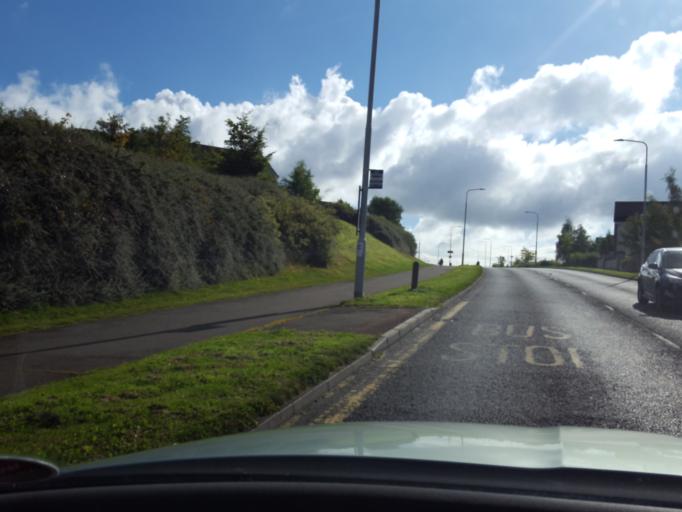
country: GB
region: Scotland
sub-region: Fife
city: Crossgates
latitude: 56.0585
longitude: -3.4073
